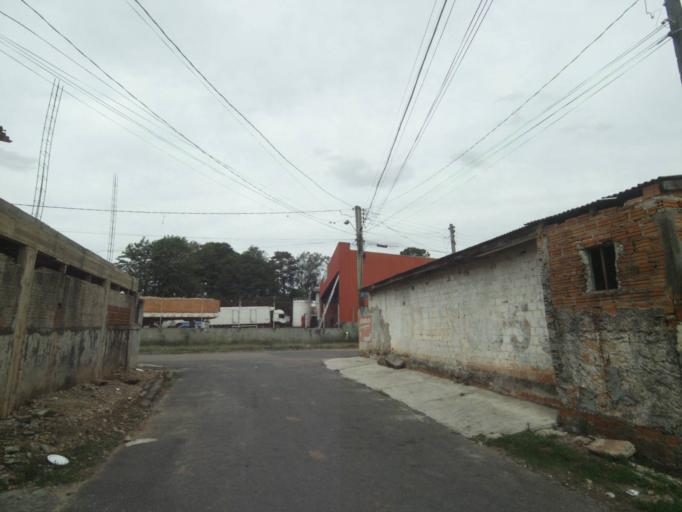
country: BR
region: Parana
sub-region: Araucaria
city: Araucaria
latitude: -25.5178
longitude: -49.3342
